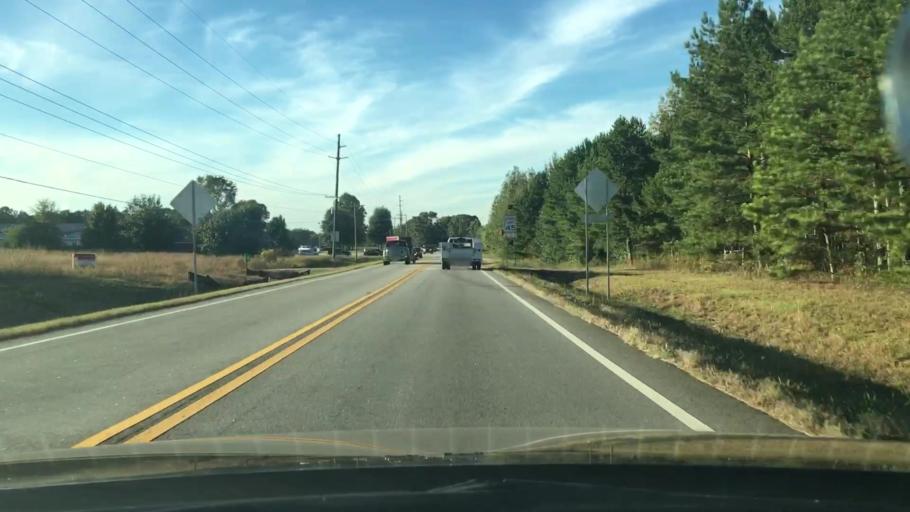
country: US
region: Georgia
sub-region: Coweta County
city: Senoia
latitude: 33.3027
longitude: -84.5956
